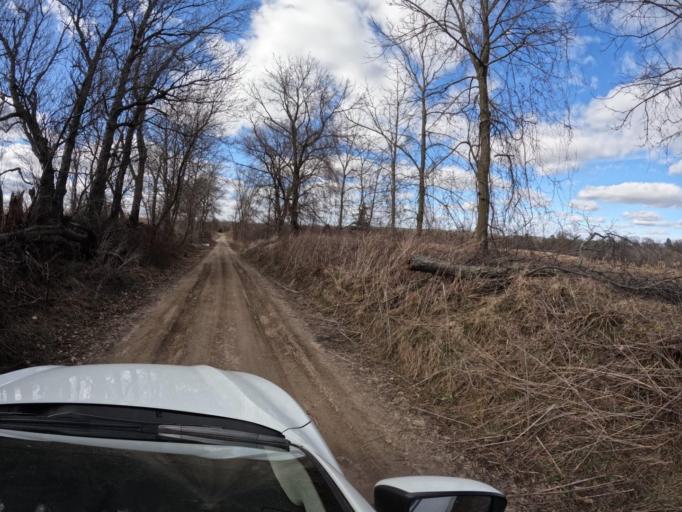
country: CA
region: Ontario
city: Norfolk County
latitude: 42.7606
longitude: -80.3162
